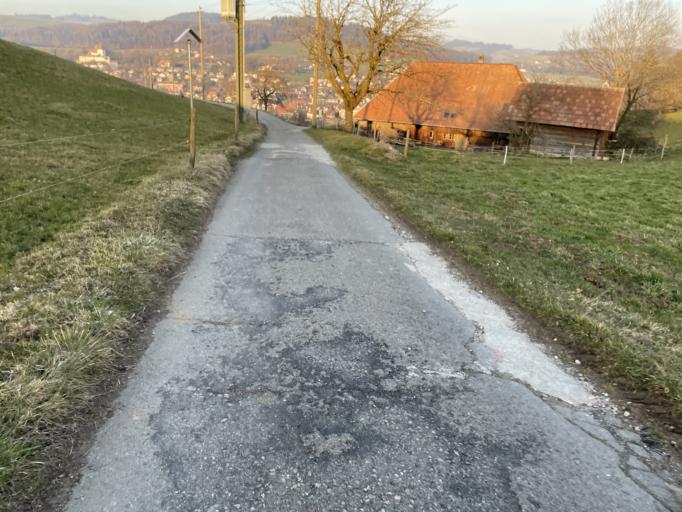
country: CH
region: Bern
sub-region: Bern-Mittelland District
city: Worb
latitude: 46.9221
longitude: 7.5588
